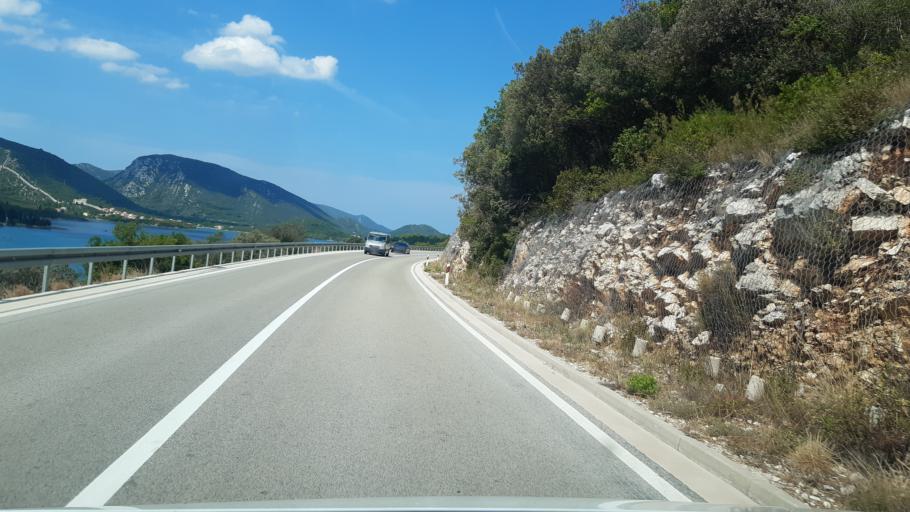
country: HR
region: Dubrovacko-Neretvanska
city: Ston
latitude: 42.8436
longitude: 17.7306
